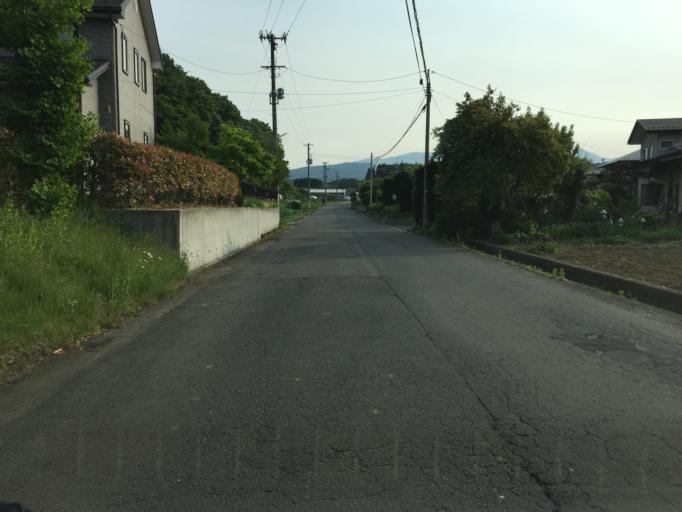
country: JP
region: Fukushima
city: Fukushima-shi
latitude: 37.7288
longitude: 140.4338
